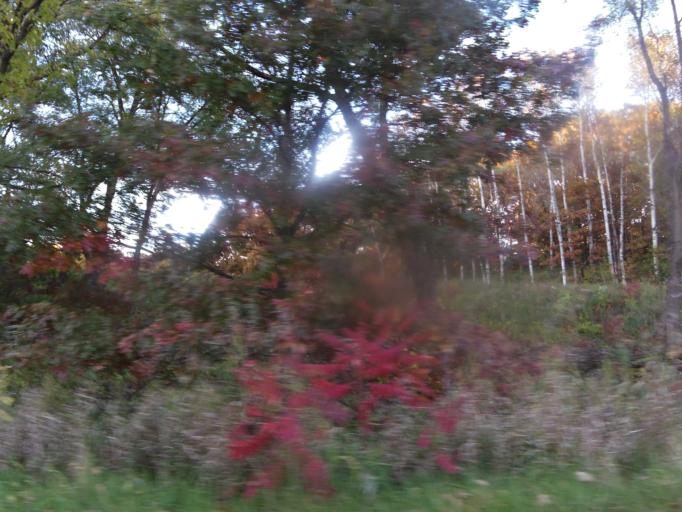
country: US
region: Minnesota
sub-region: Washington County
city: Lake Elmo
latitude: 44.9764
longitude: -92.8762
